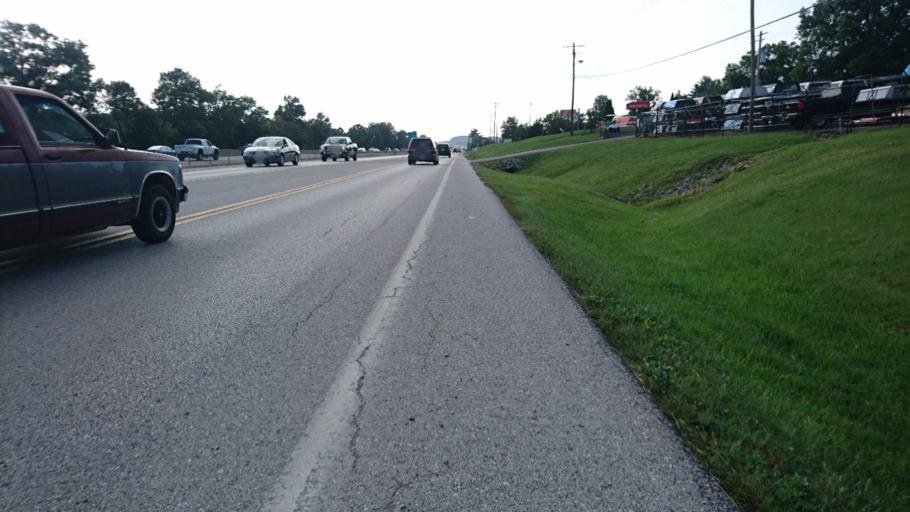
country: US
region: Missouri
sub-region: Saint Louis County
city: Eureka
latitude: 38.5044
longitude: -90.6520
